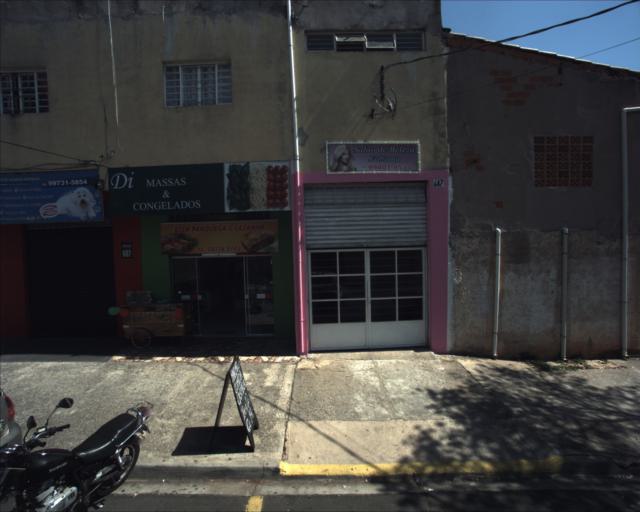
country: BR
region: Sao Paulo
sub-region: Sorocaba
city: Sorocaba
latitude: -23.5018
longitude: -47.5169
